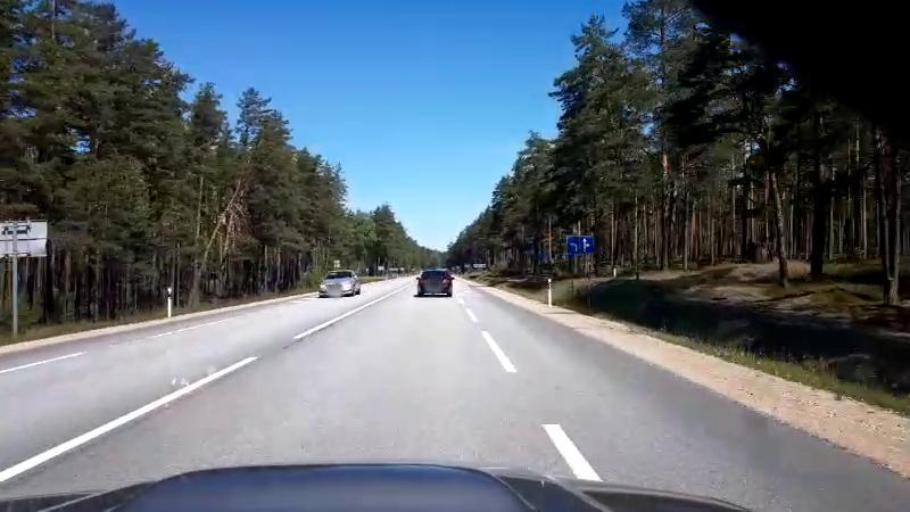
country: LV
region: Carnikava
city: Carnikava
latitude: 57.1735
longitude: 24.3430
